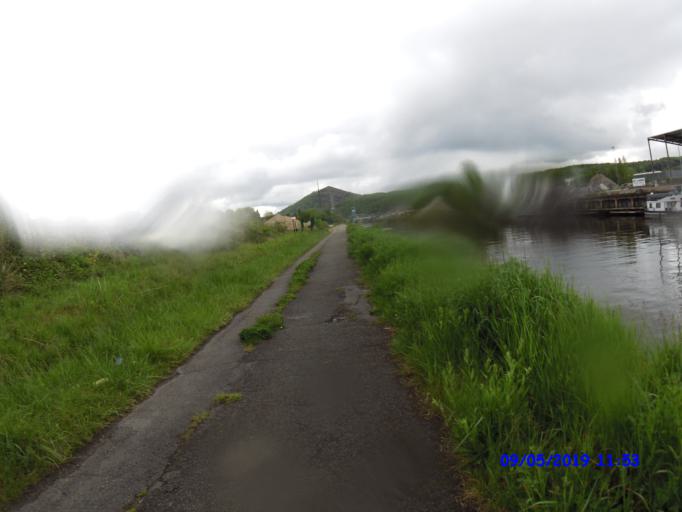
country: BE
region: Wallonia
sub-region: Province du Hainaut
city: Charleroi
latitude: 50.3983
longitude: 4.4693
